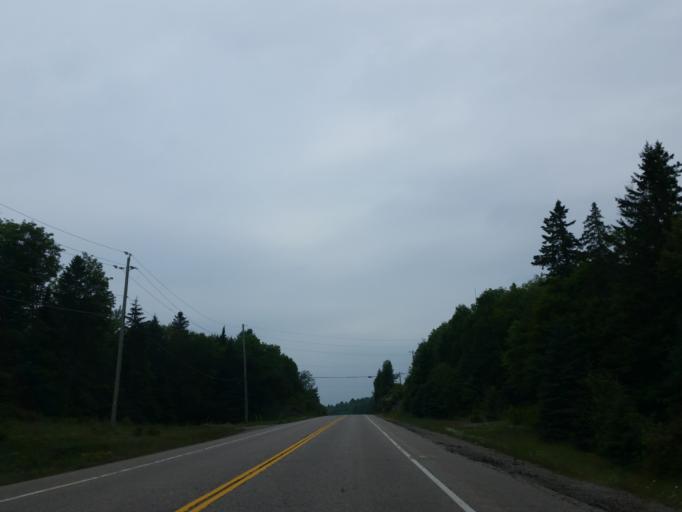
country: CA
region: Ontario
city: Mattawa
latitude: 45.5804
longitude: -78.4595
